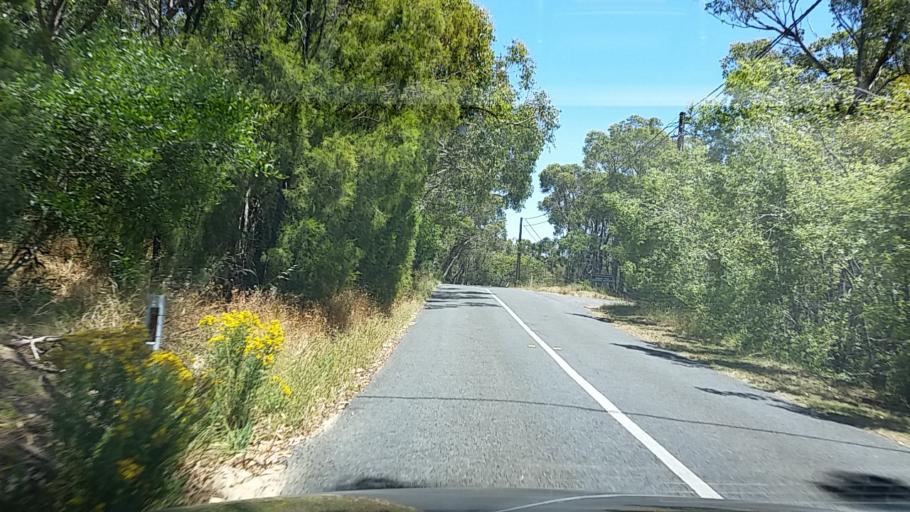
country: AU
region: South Australia
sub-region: Adelaide Hills
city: Crafers
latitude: -34.9901
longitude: 138.6823
